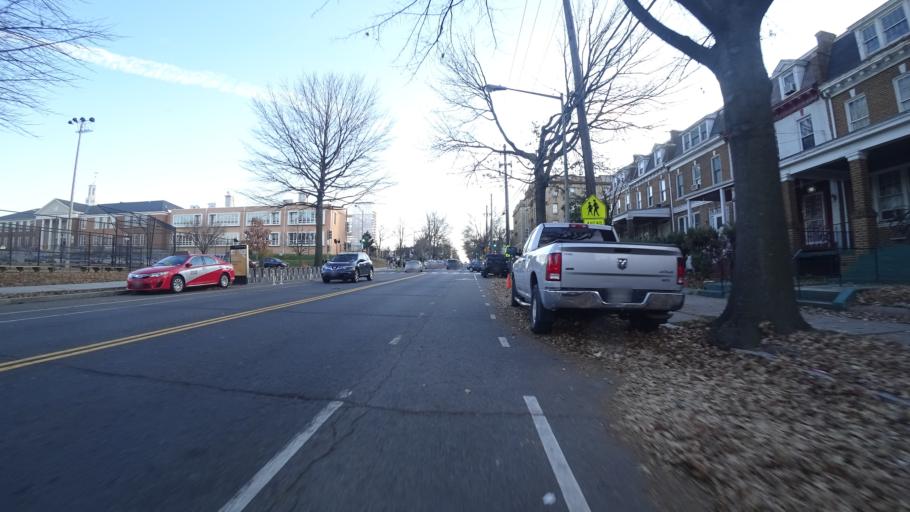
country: US
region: Maryland
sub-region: Montgomery County
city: Takoma Park
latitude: 38.9424
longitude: -77.0328
